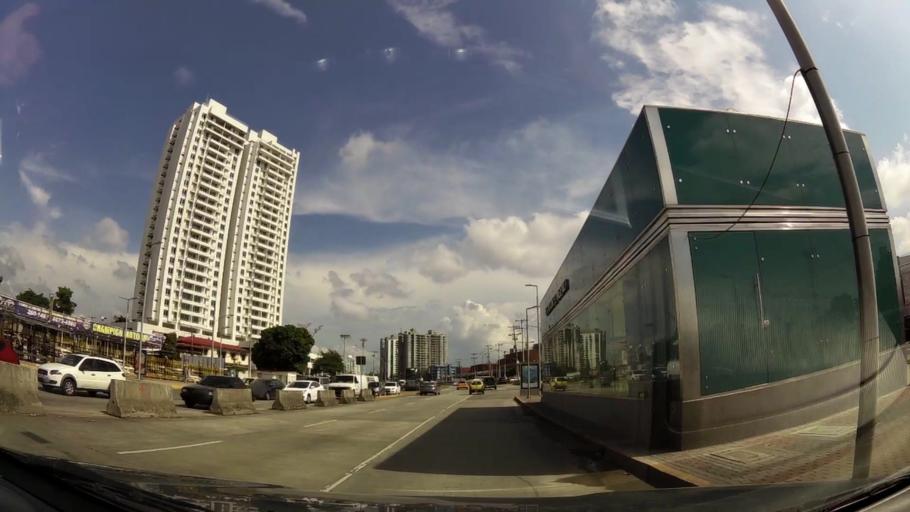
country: PA
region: Panama
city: Panama
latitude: 9.0078
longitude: -79.5191
